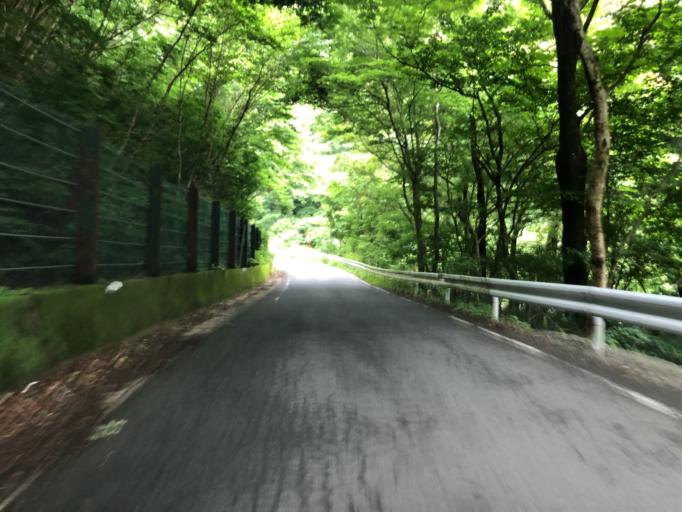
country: JP
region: Fukushima
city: Namie
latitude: 37.6871
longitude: 140.8751
